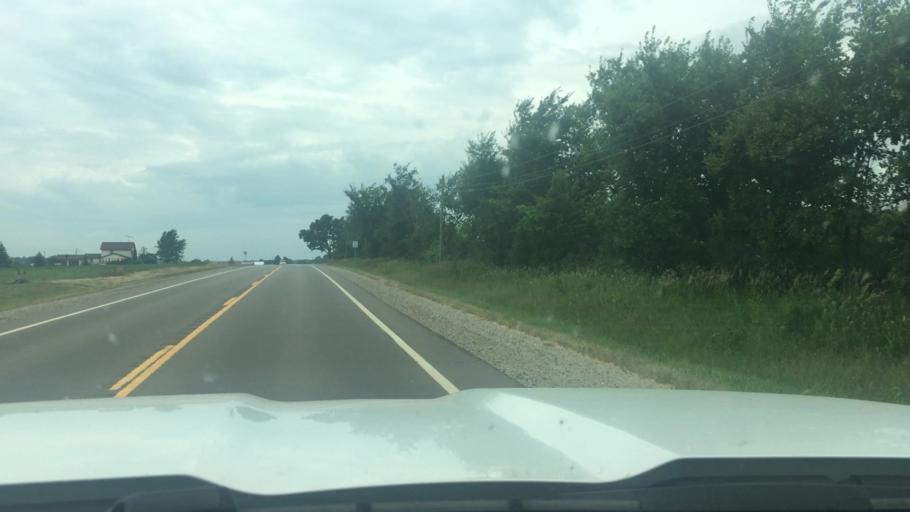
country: US
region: Michigan
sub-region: Clinton County
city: Fowler
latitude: 43.0018
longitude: -84.7713
